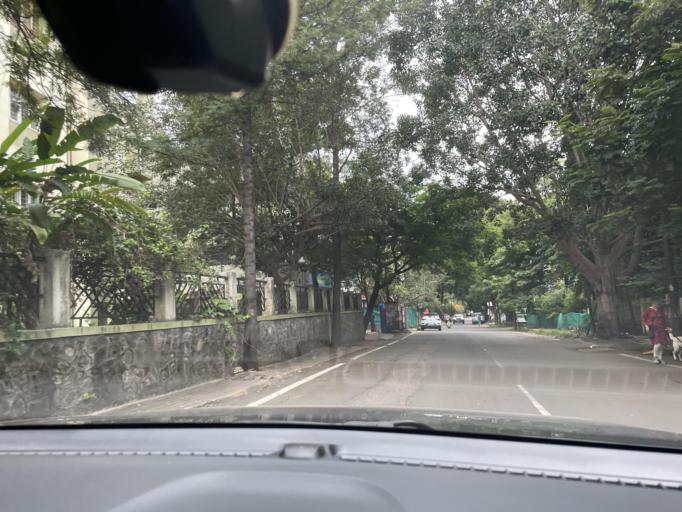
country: IN
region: Maharashtra
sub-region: Pune Division
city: Shivaji Nagar
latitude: 18.5338
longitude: 73.8113
